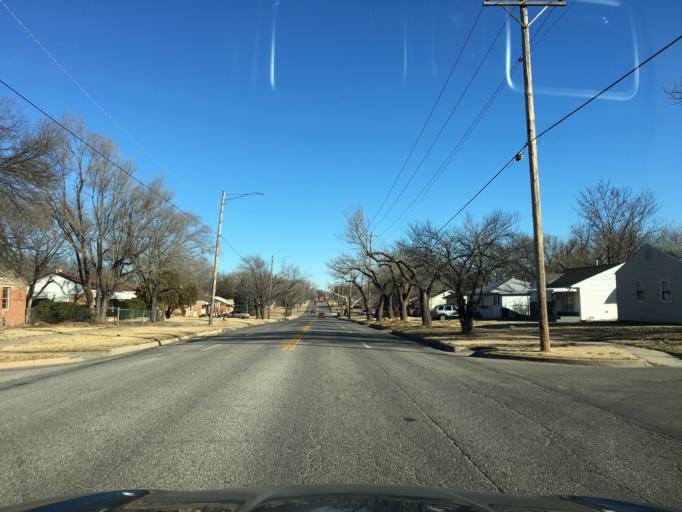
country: US
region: Kansas
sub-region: Sedgwick County
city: Wichita
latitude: 37.6719
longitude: -97.2528
